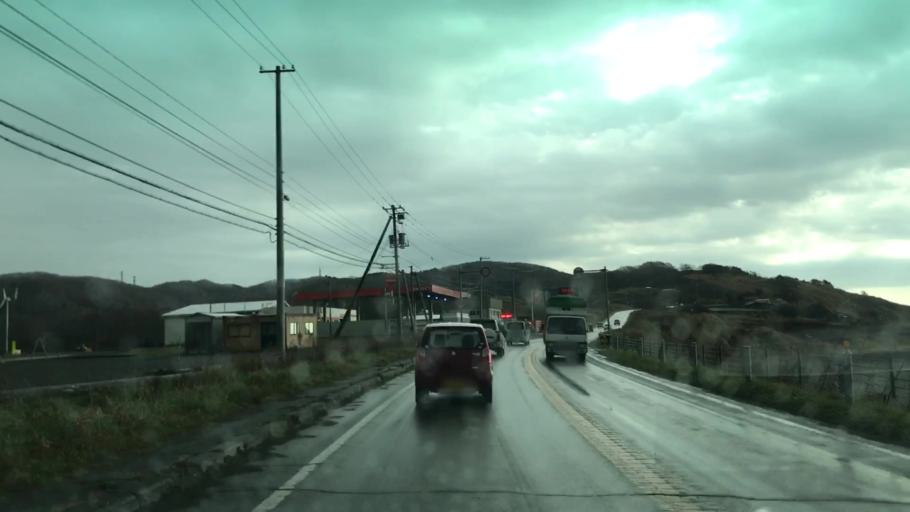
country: JP
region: Hokkaido
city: Shizunai-furukawacho
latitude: 42.1856
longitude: 142.7214
